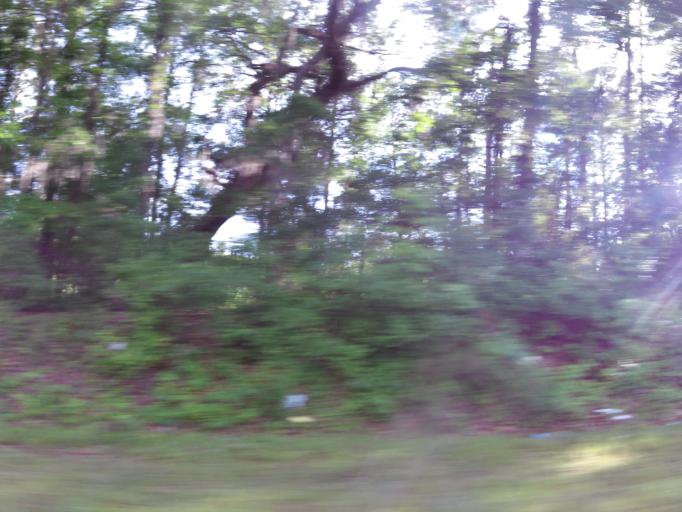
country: US
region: South Carolina
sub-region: Hampton County
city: Estill
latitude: 32.5906
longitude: -81.2047
